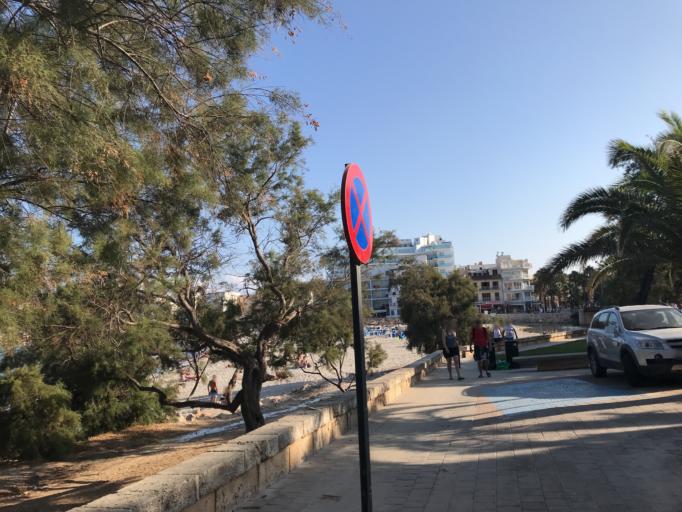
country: ES
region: Balearic Islands
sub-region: Illes Balears
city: Son Servera
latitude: 39.5673
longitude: 3.3731
